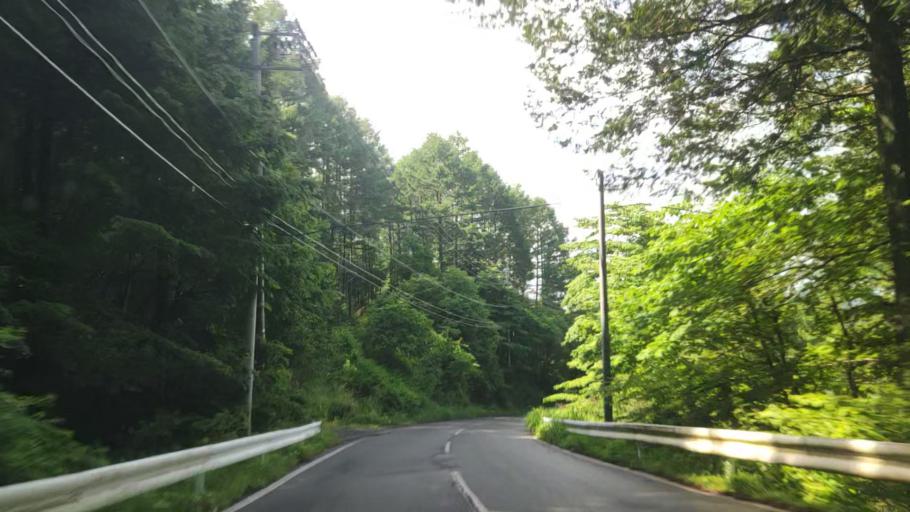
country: JP
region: Nagano
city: Suwa
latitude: 36.0741
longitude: 138.1377
